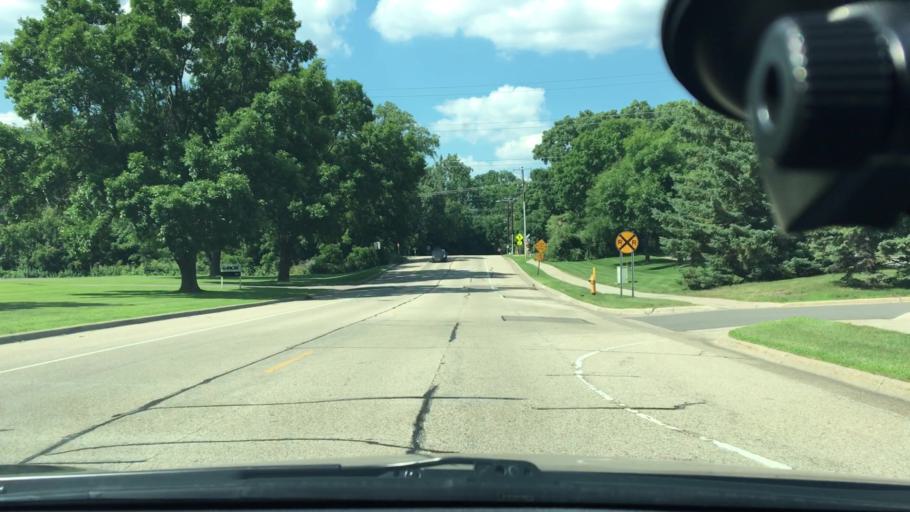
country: US
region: Minnesota
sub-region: Hennepin County
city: Golden Valley
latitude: 44.9899
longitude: -93.3903
